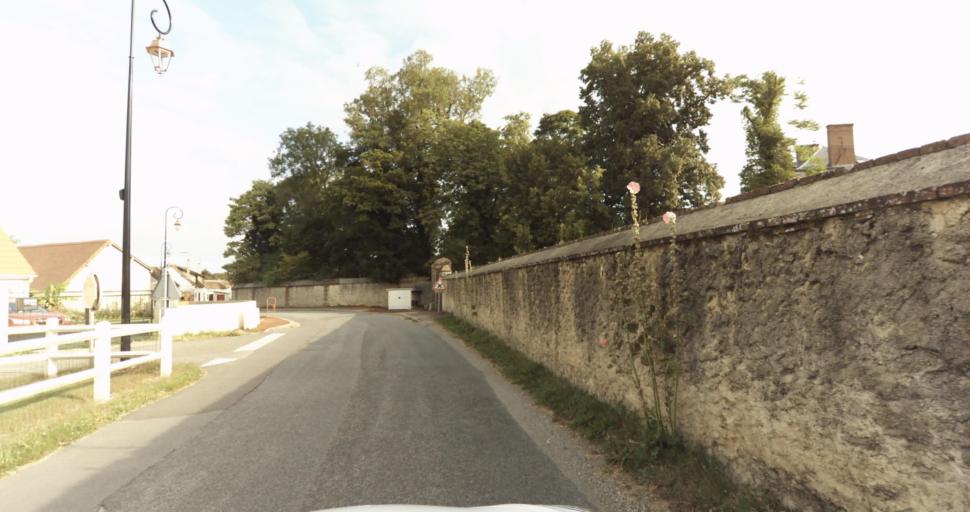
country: FR
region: Centre
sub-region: Departement d'Eure-et-Loir
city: Vert-en-Drouais
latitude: 48.7716
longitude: 1.3032
